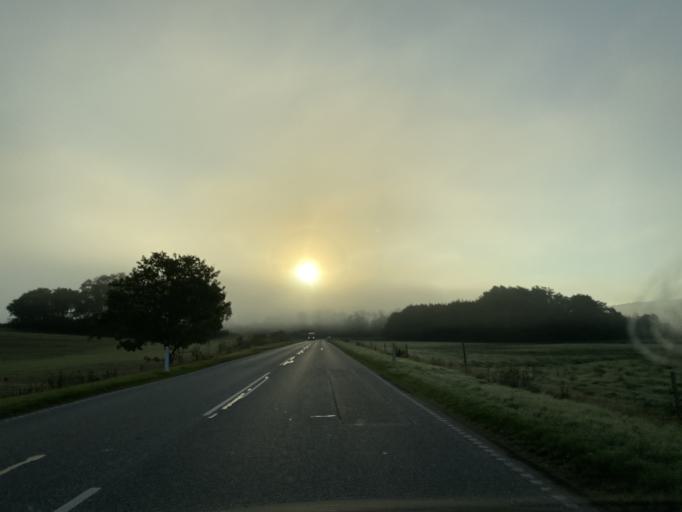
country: DK
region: Central Jutland
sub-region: Skanderborg Kommune
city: Galten
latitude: 56.1141
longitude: 9.8722
